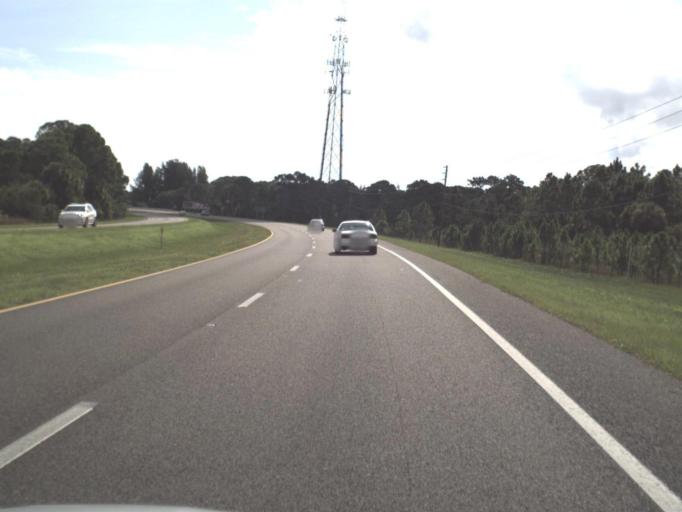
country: US
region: Florida
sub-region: Sarasota County
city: Warm Mineral Springs
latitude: 27.0426
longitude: -82.3062
